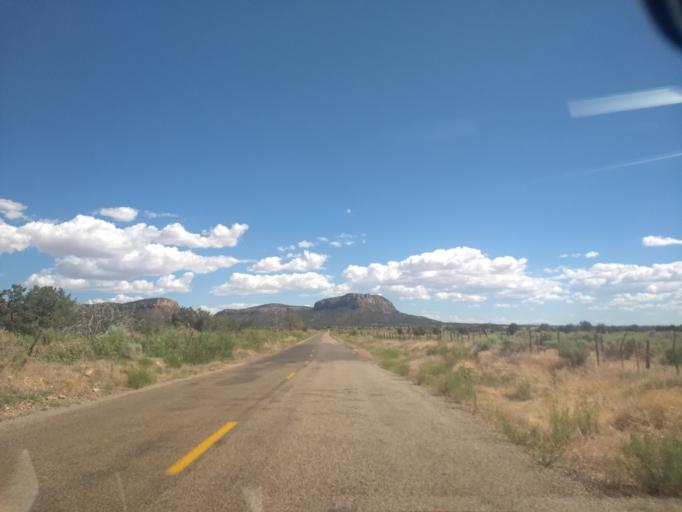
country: US
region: Utah
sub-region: Washington County
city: Hildale
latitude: 36.9536
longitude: -112.8746
